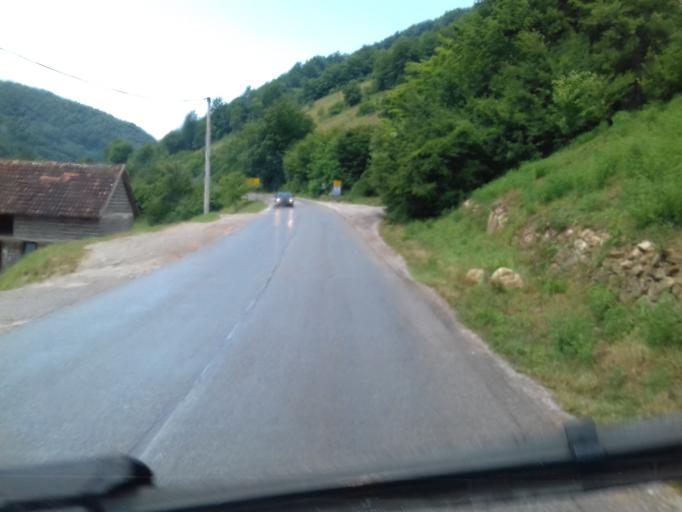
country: BA
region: Federation of Bosnia and Herzegovina
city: Kiseljak
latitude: 43.9553
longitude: 18.1055
